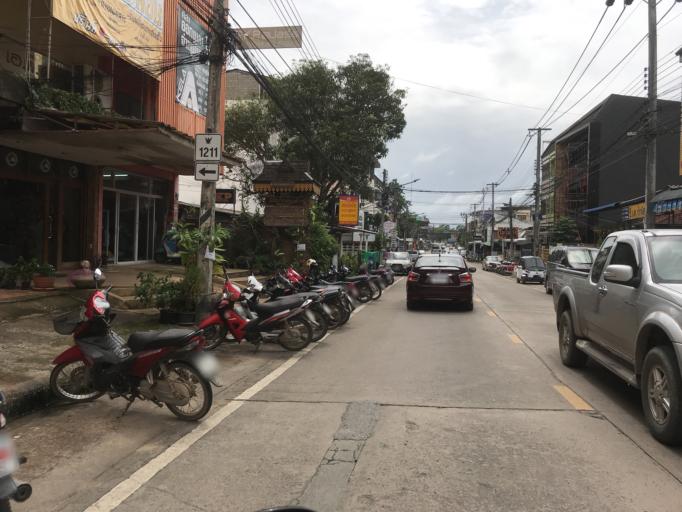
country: TH
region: Chiang Rai
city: Chiang Rai
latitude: 19.9022
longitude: 99.8167
